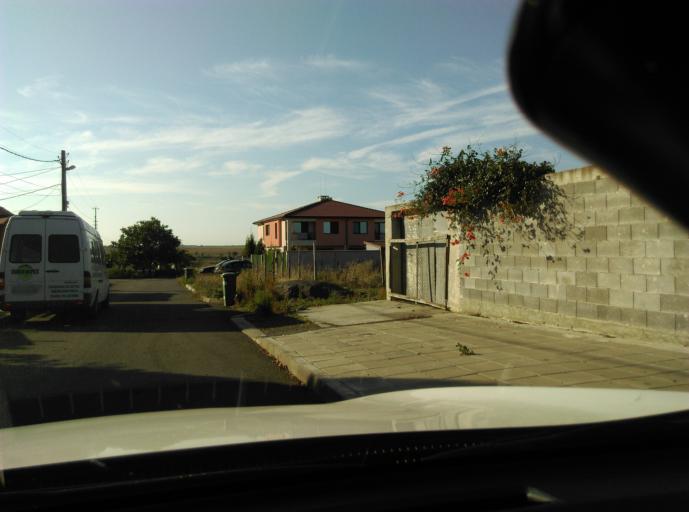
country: BG
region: Burgas
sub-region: Obshtina Kameno
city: Kameno
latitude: 42.5982
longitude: 27.3832
